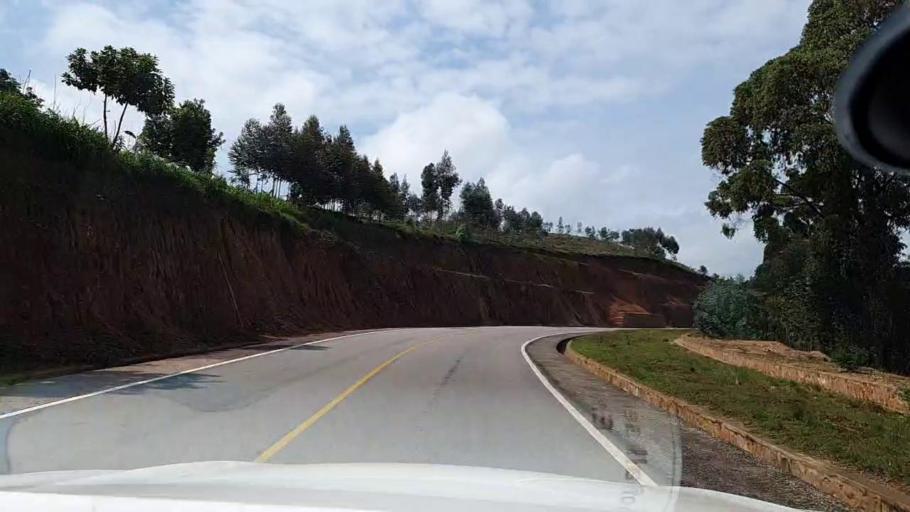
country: RW
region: Southern Province
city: Nzega
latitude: -2.4913
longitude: 29.5113
